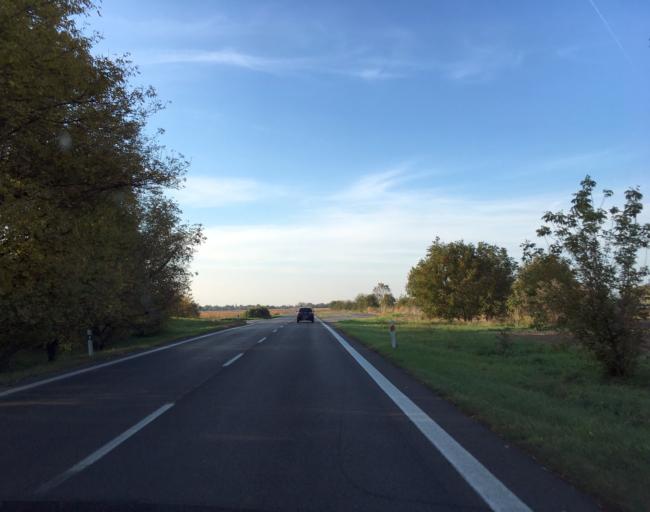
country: SK
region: Nitriansky
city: Sellye
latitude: 48.1571
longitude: 17.9121
